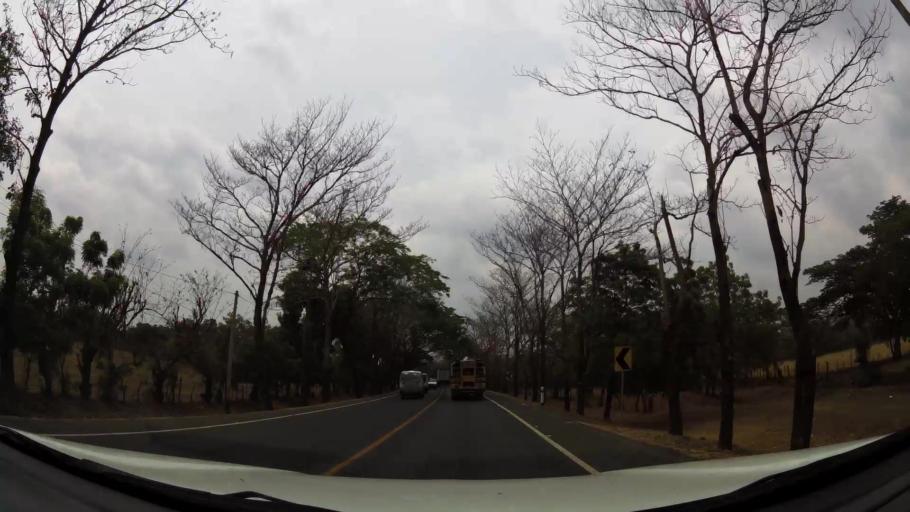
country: NI
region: Leon
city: Telica
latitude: 12.5120
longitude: -86.8609
